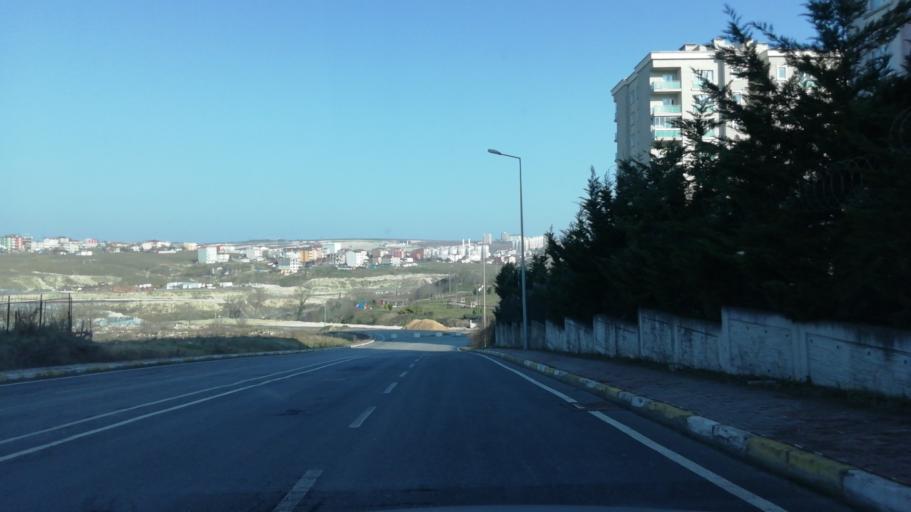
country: TR
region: Istanbul
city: Esenyurt
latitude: 41.1116
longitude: 28.6416
